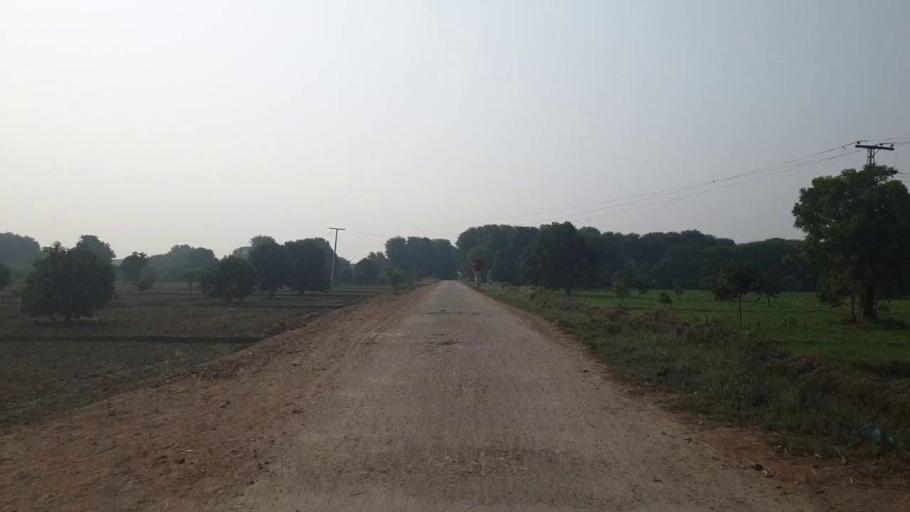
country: PK
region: Sindh
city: Tando Jam
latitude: 25.3250
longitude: 68.5181
